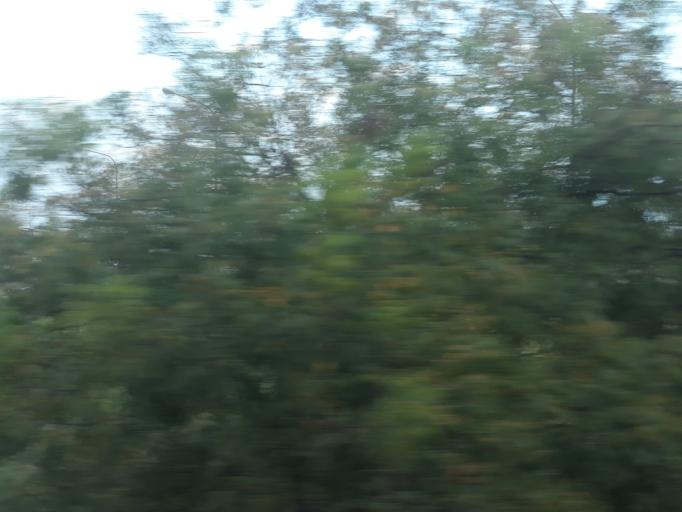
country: TW
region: Taiwan
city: Xinying
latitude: 23.1810
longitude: 120.2336
